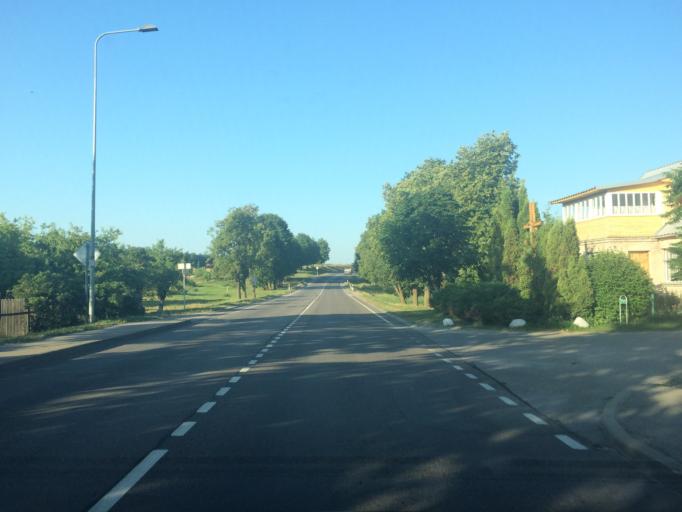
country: LT
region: Vilnius County
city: Ukmerge
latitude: 55.3036
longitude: 24.8612
